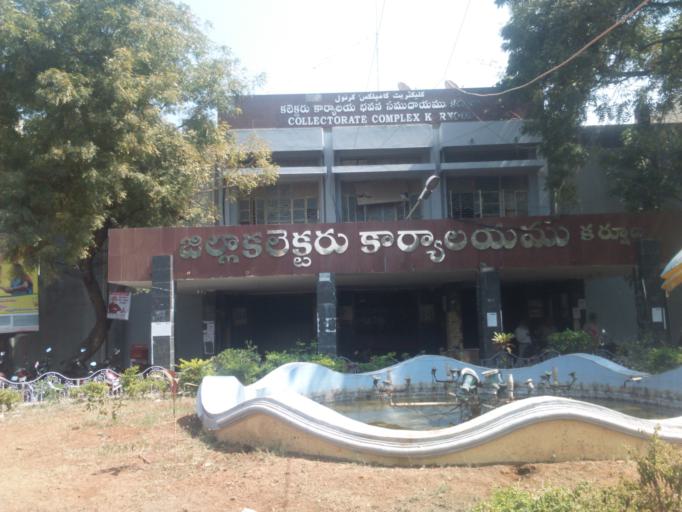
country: IN
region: Telangana
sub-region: Mahbubnagar
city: Alampur
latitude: 15.8179
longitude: 78.0415
